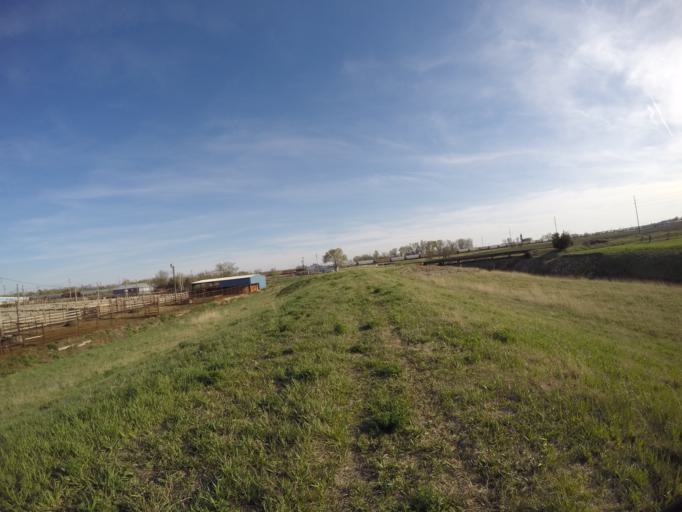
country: US
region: Kansas
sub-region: Saline County
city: Salina
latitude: 38.8461
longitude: -97.6305
